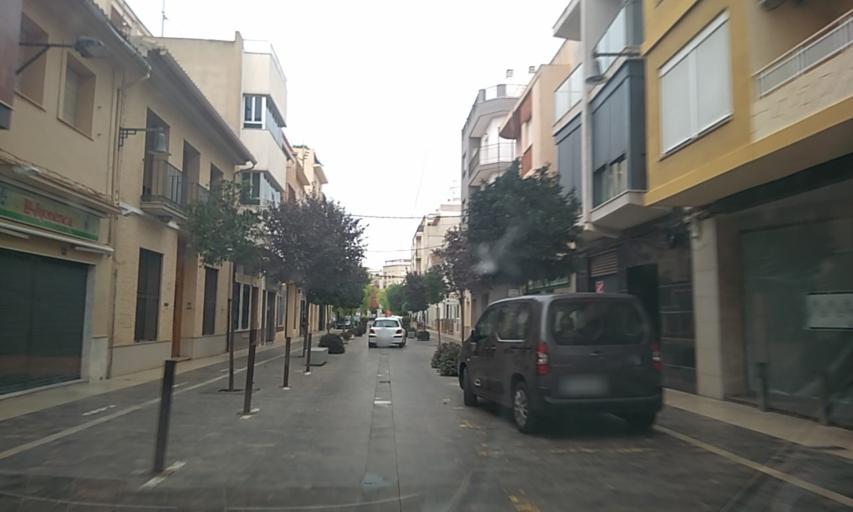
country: ES
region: Valencia
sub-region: Provincia de Valencia
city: L'Alcudia
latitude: 39.1967
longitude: -0.5073
